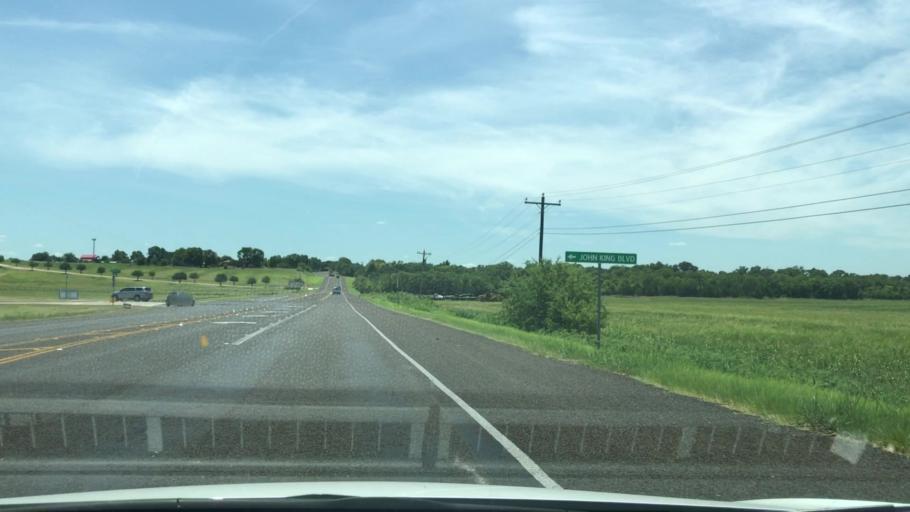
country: US
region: Texas
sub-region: Rockwall County
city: Rockwall
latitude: 32.9804
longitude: -96.4668
